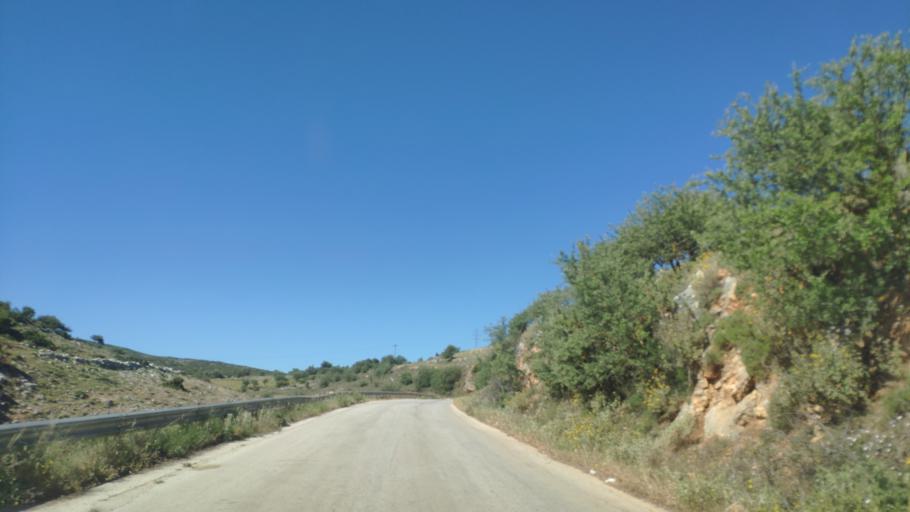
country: GR
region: Peloponnese
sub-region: Nomos Korinthias
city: Khiliomodhi
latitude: 37.7567
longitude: 22.8754
